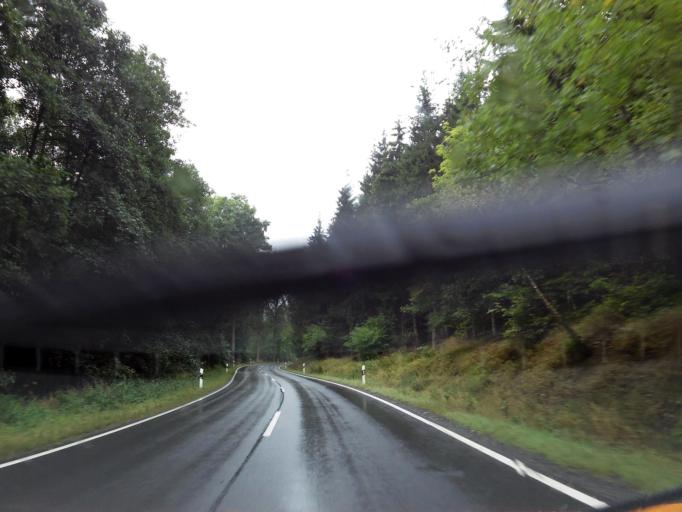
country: DE
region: Saxony-Anhalt
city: Harzgerode
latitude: 51.6777
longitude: 11.1373
